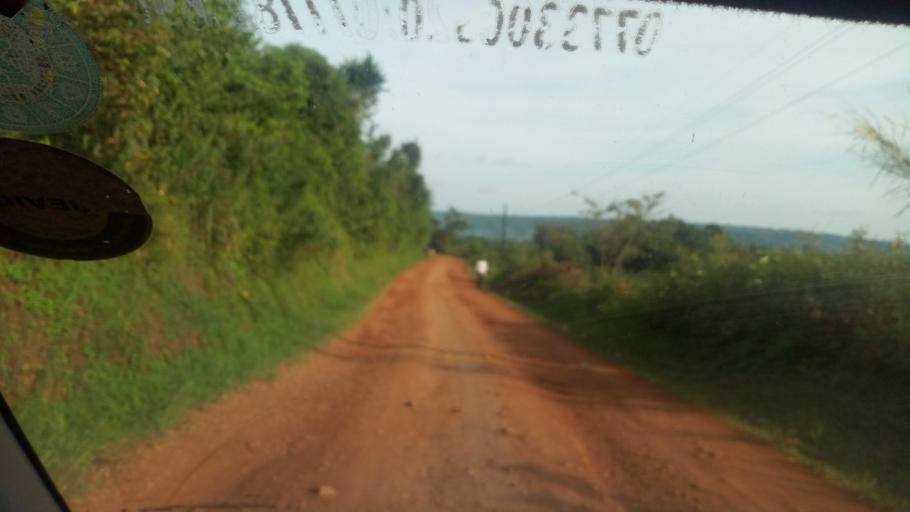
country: UG
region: Central Region
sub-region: Buikwe District
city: Buikwe
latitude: 0.2270
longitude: 32.9246
